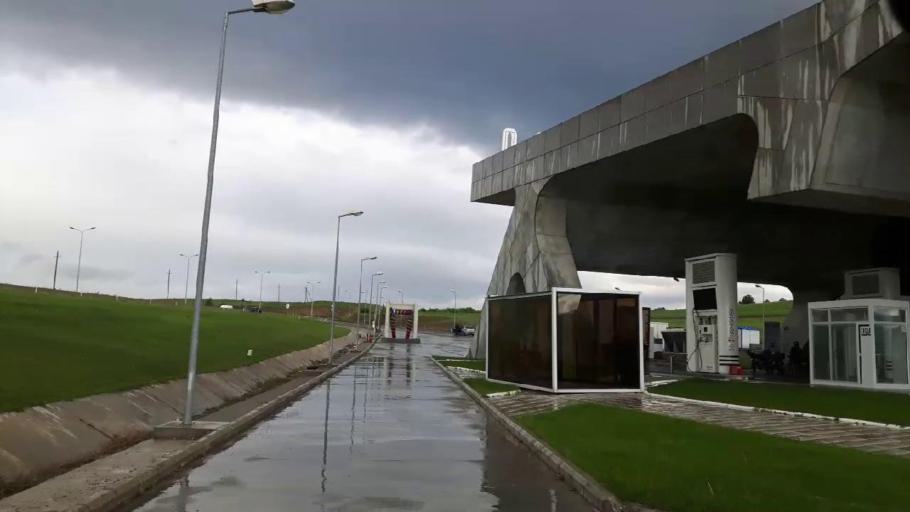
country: GE
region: Shida Kartli
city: Gori
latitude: 42.0156
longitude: 44.0303
